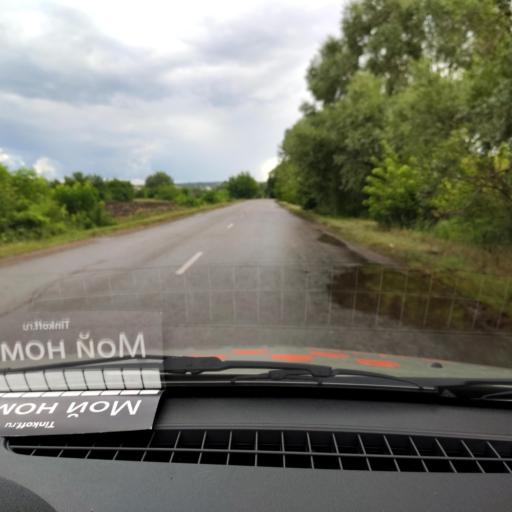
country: RU
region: Bashkortostan
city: Avdon
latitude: 54.5058
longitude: 55.8778
